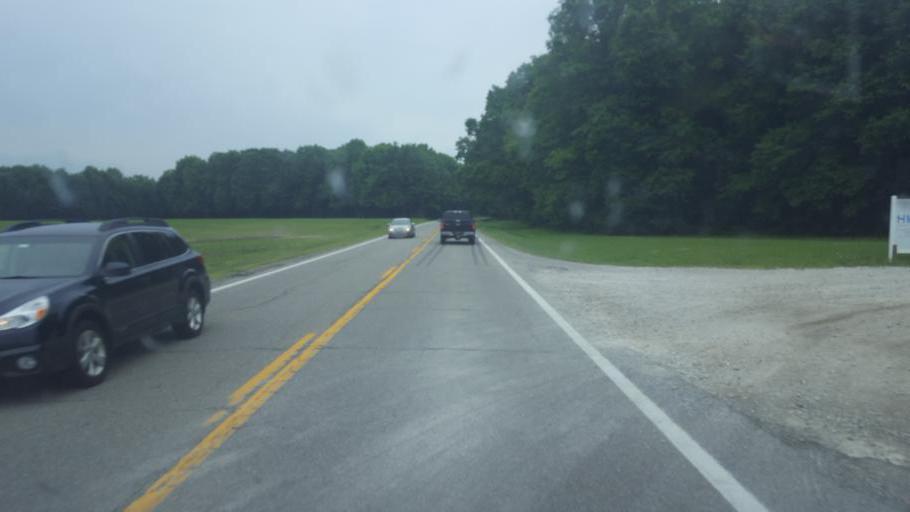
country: US
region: Ohio
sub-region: Trumbull County
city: Newton Falls
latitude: 41.1958
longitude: -80.9987
